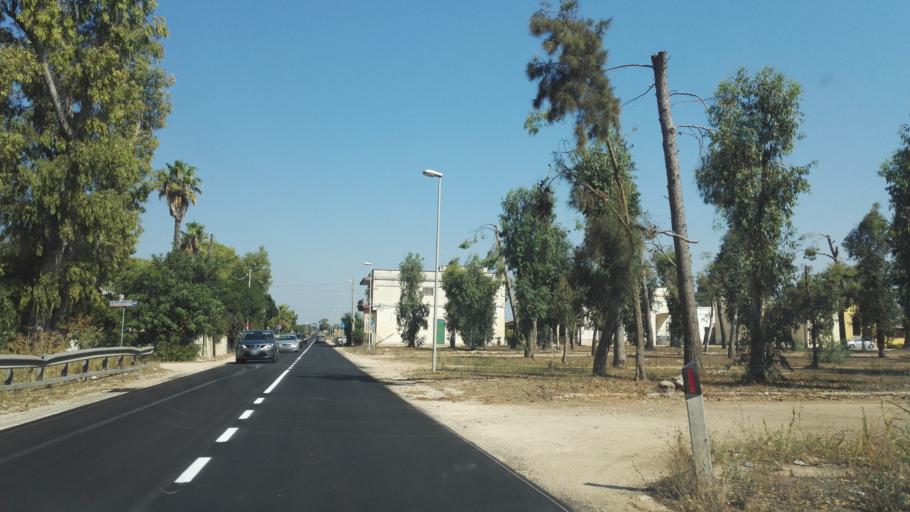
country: IT
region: Apulia
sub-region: Provincia di Lecce
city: Nardo
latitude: 40.2017
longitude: 17.9580
